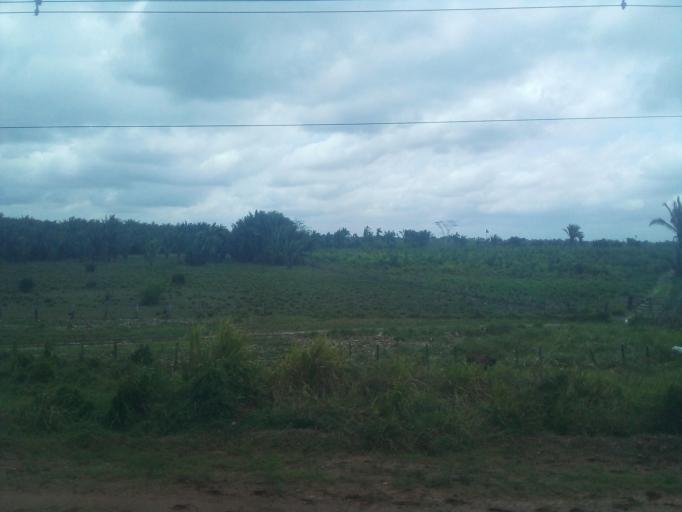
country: BR
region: Maranhao
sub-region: Pindare Mirim
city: Pindare Mirim
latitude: -3.6729
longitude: -45.3041
